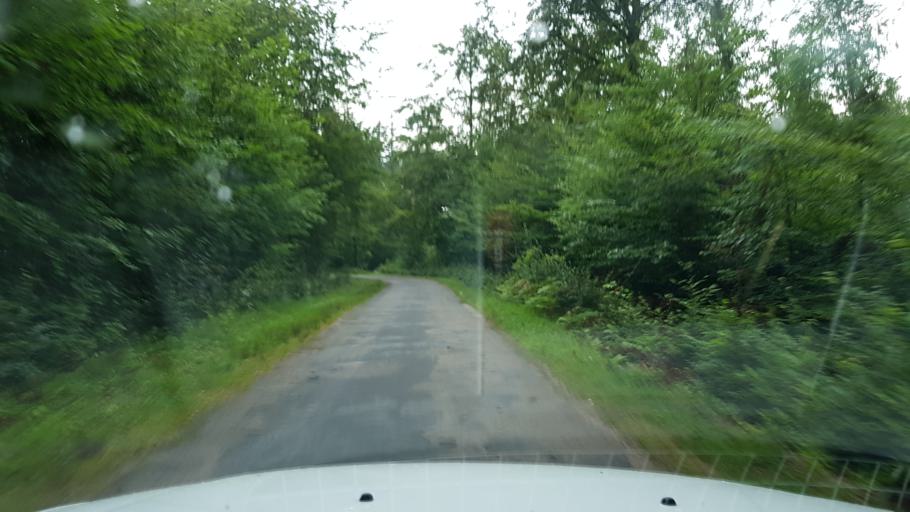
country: PL
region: West Pomeranian Voivodeship
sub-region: Powiat koszalinski
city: Bobolice
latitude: 53.8946
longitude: 16.6769
